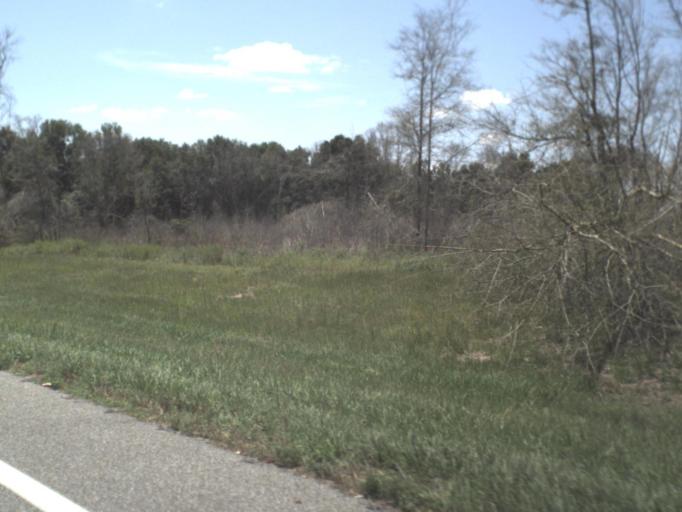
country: US
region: Florida
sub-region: Lafayette County
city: Mayo
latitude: 30.0533
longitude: -83.1173
